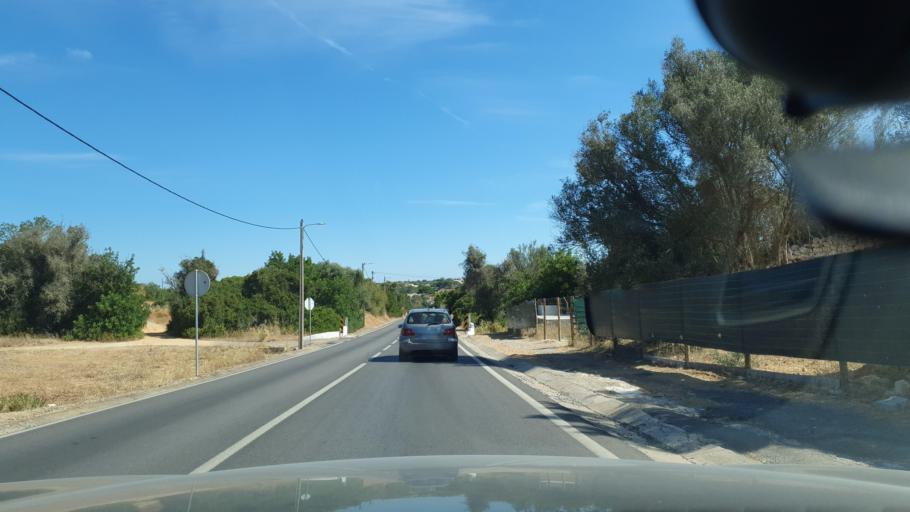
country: PT
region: Faro
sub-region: Albufeira
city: Guia
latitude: 37.1053
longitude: -8.3081
